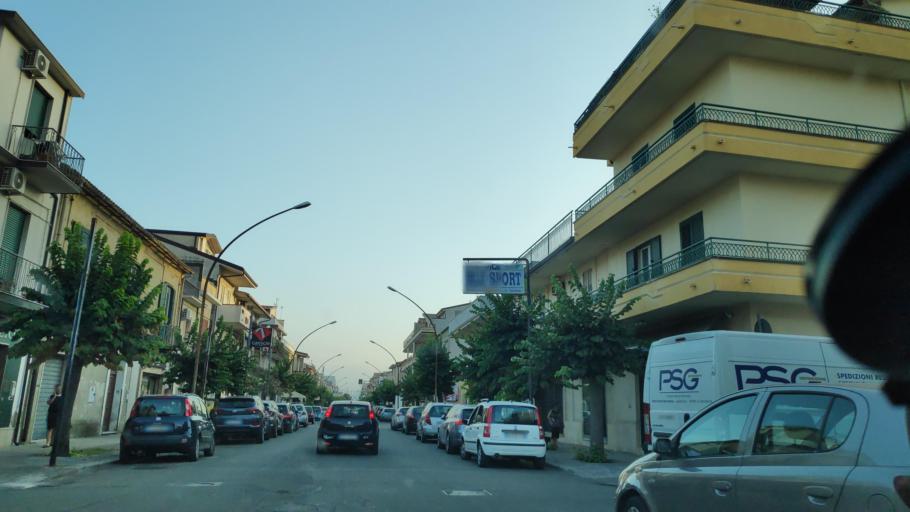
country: IT
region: Calabria
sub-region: Provincia di Reggio Calabria
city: Siderno
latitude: 38.2682
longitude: 16.2954
